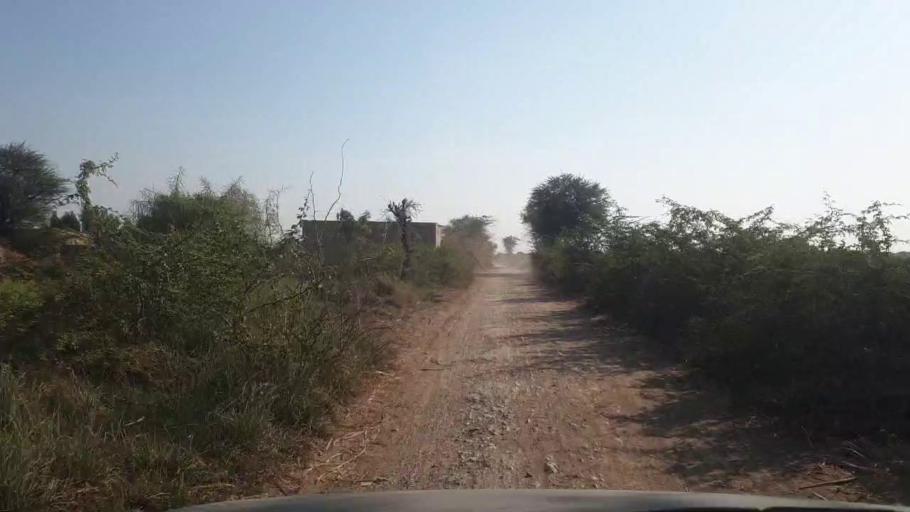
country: PK
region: Sindh
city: Chambar
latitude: 25.2872
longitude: 68.8515
